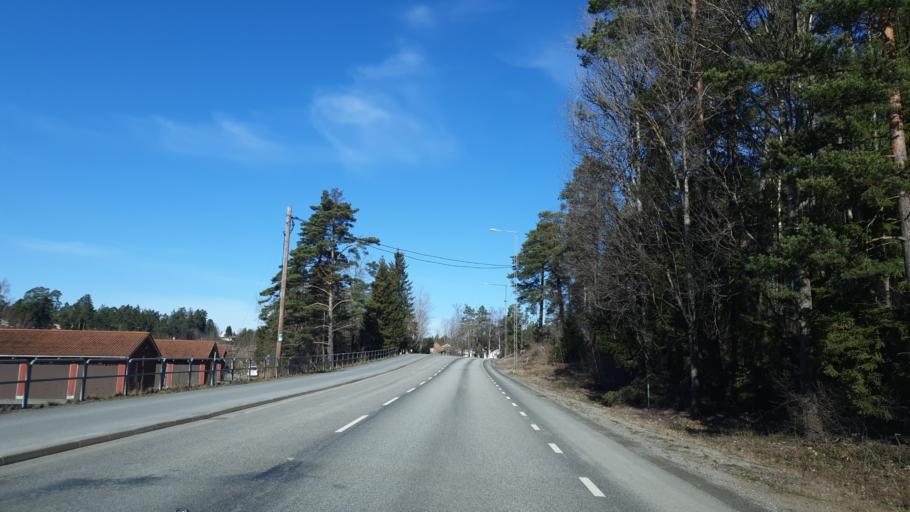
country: SE
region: Stockholm
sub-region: Jarfalla Kommun
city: Jakobsberg
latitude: 59.4422
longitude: 17.8392
